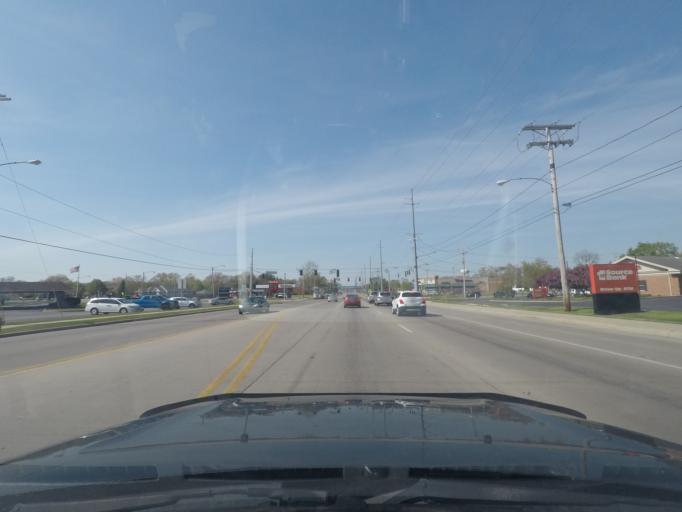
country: US
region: Indiana
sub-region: Elkhart County
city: Elkhart
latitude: 41.6819
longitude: -86.0033
